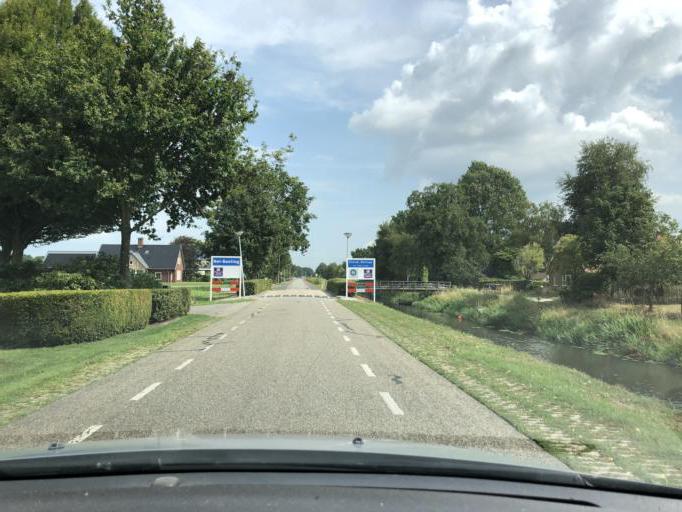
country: NL
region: Drenthe
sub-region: Gemeente Hoogeveen
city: Hoogeveen
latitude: 52.7608
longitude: 6.6031
